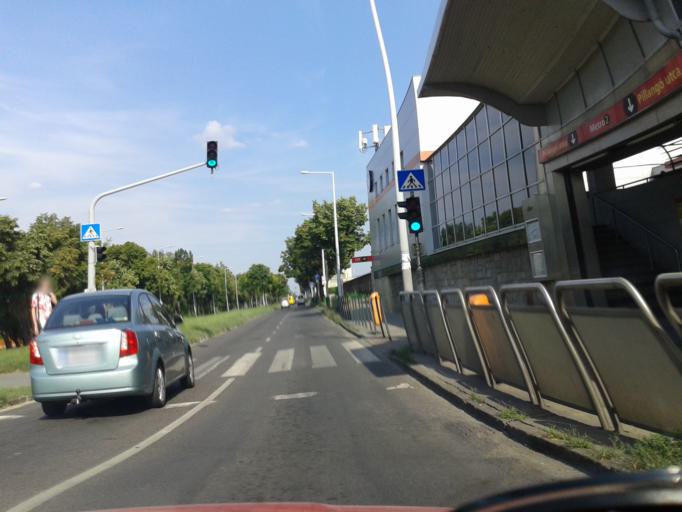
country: HU
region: Budapest
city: Budapest XIV. keruelet
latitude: 47.5013
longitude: 19.1198
